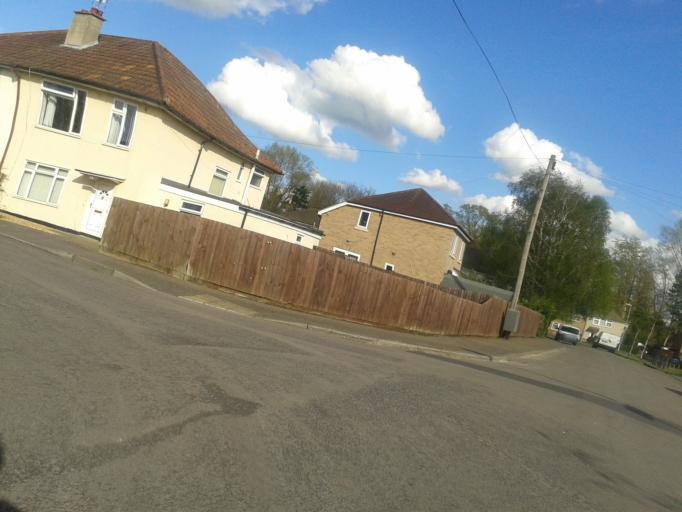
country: GB
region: England
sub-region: Cambridgeshire
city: Cambridge
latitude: 52.1878
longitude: 0.1608
